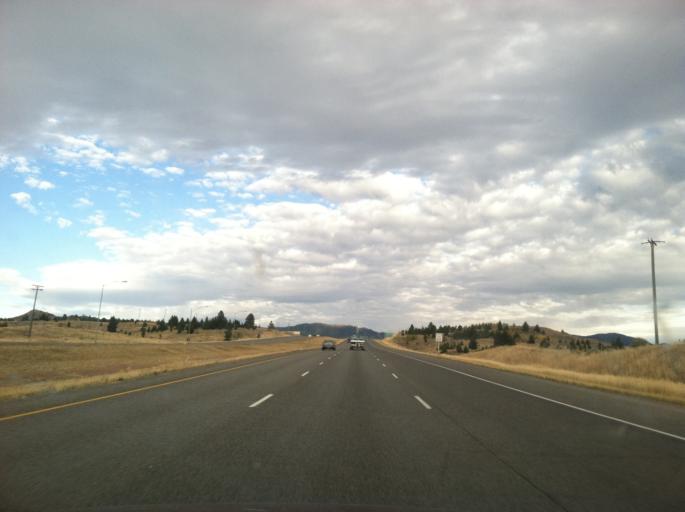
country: US
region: Montana
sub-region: Silver Bow County
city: Butte
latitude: 46.0062
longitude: -112.6035
